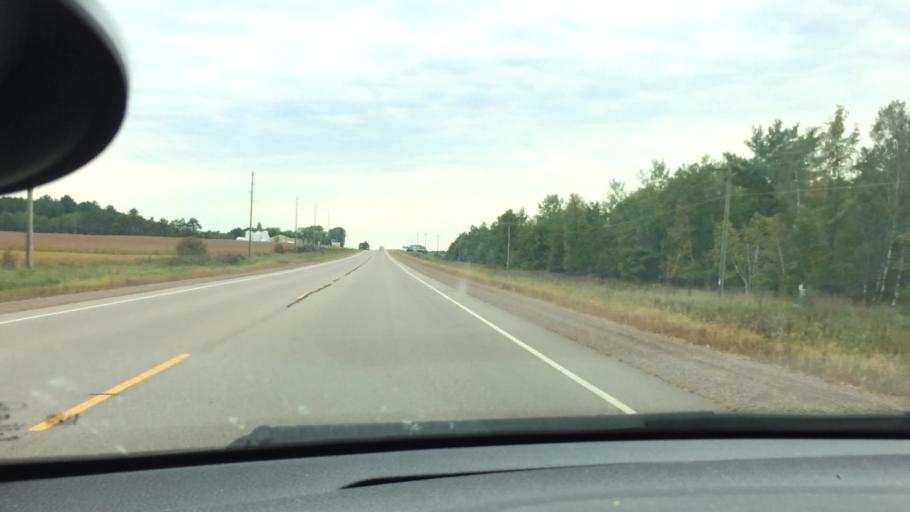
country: US
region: Wisconsin
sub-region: Eau Claire County
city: Augusta
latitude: 44.5964
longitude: -90.9272
